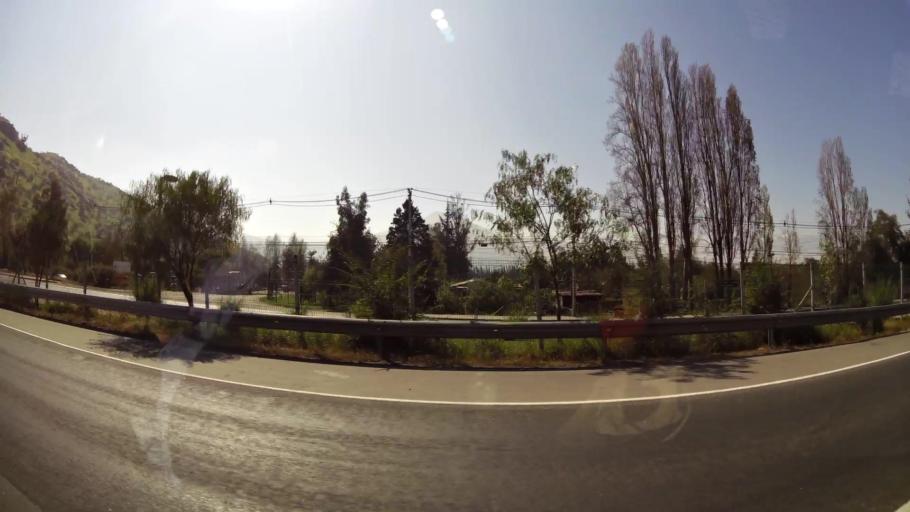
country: CL
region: Santiago Metropolitan
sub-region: Provincia de Chacabuco
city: Chicureo Abajo
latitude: -33.3540
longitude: -70.6923
